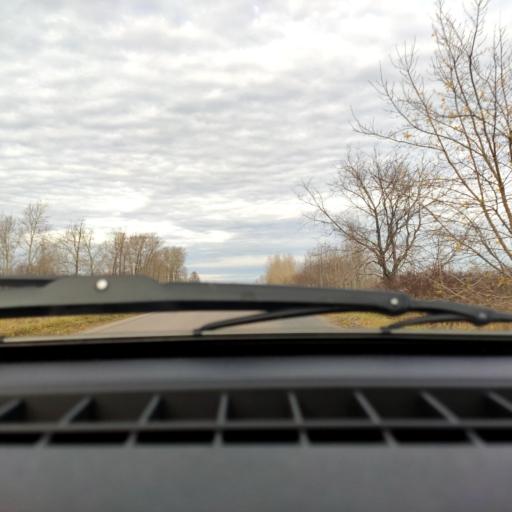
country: RU
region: Bashkortostan
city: Ufa
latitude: 54.8824
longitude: 56.1340
